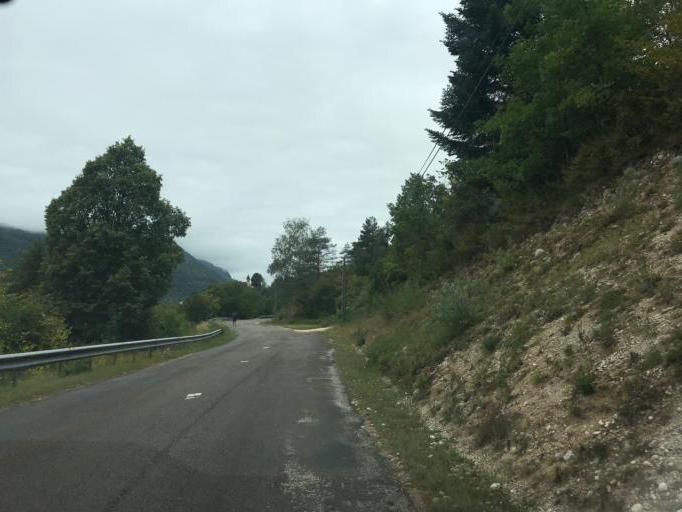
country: FR
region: Rhone-Alpes
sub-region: Departement de l'Ain
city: Dortan
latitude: 46.3428
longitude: 5.6268
